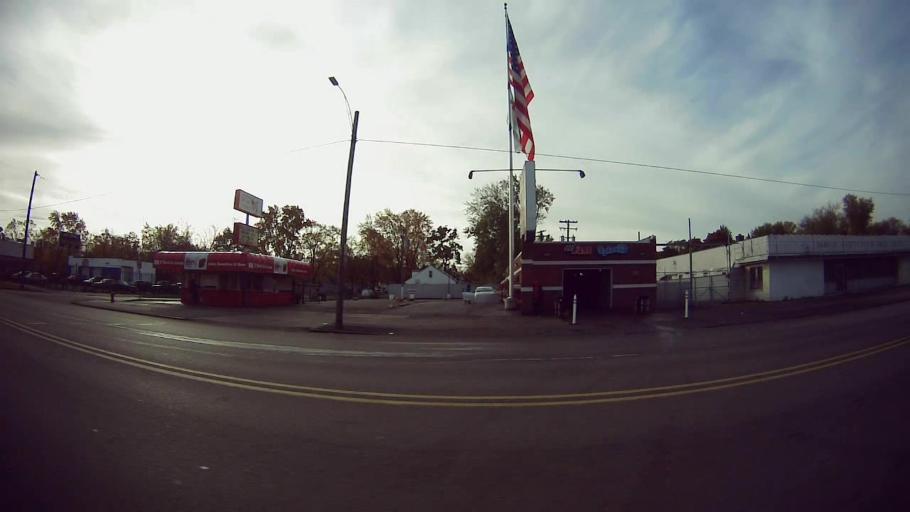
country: US
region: Michigan
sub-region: Oakland County
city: Southfield
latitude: 42.4294
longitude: -83.2478
